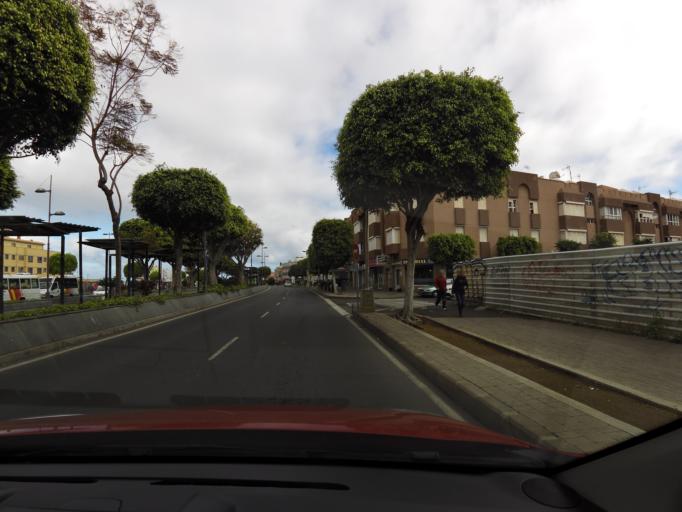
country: ES
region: Canary Islands
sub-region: Provincia de Las Palmas
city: Telde
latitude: 27.9989
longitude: -15.4182
